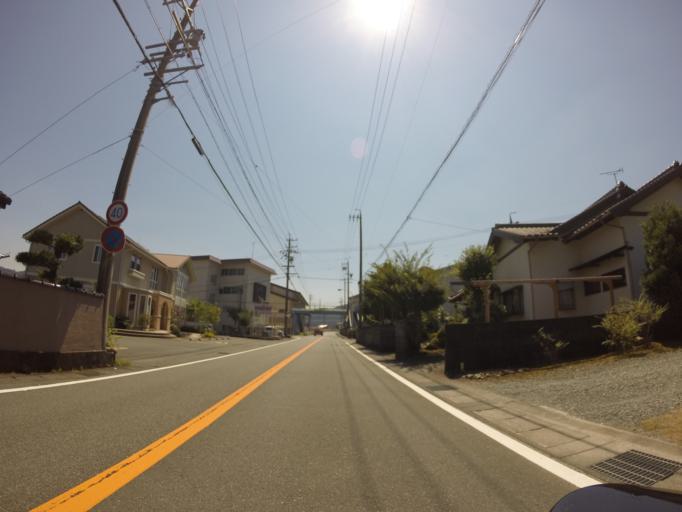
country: JP
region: Shizuoka
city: Fujinomiya
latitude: 35.1847
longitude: 138.5969
